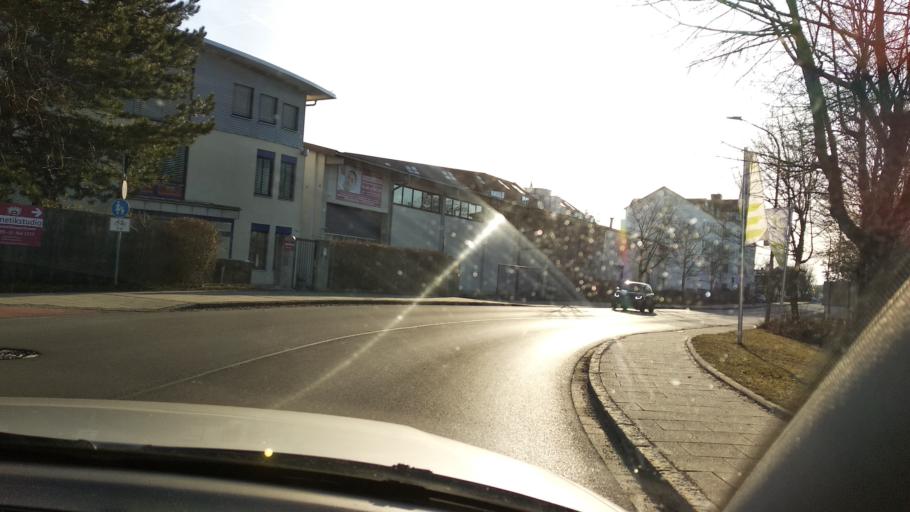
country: DE
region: Bavaria
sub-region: Upper Bavaria
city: Taufkirchen
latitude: 48.0563
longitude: 11.6110
